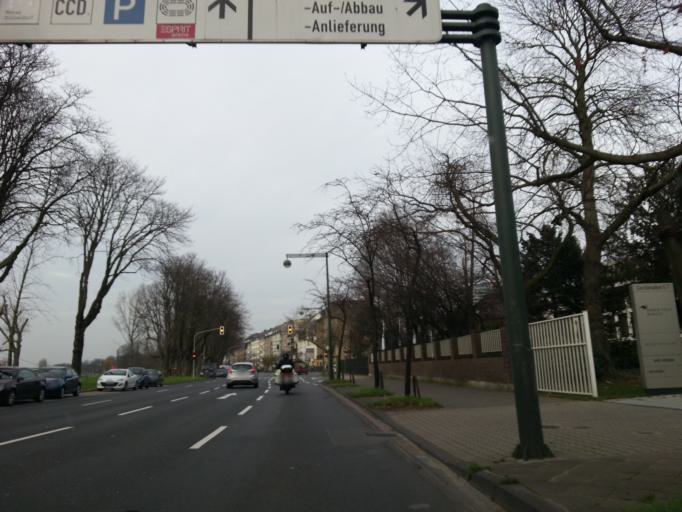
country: DE
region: North Rhine-Westphalia
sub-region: Regierungsbezirk Dusseldorf
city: Dusseldorf
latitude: 51.2408
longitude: 6.7712
